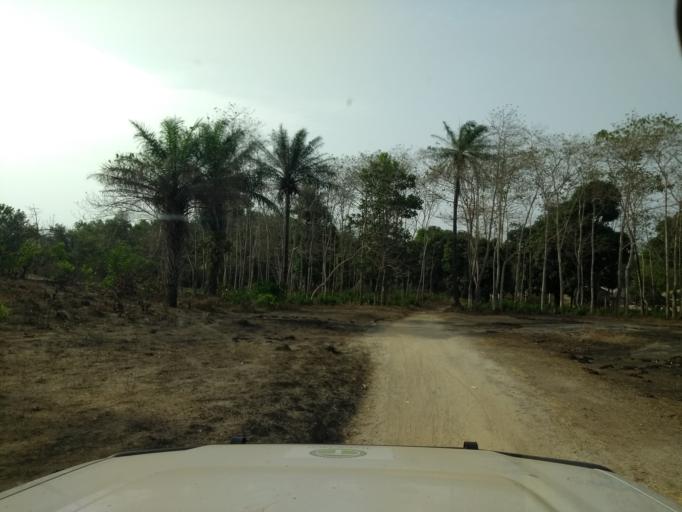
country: GN
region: Kindia
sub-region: Prefecture de Dubreka
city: Dubreka
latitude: 9.8304
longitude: -13.5563
